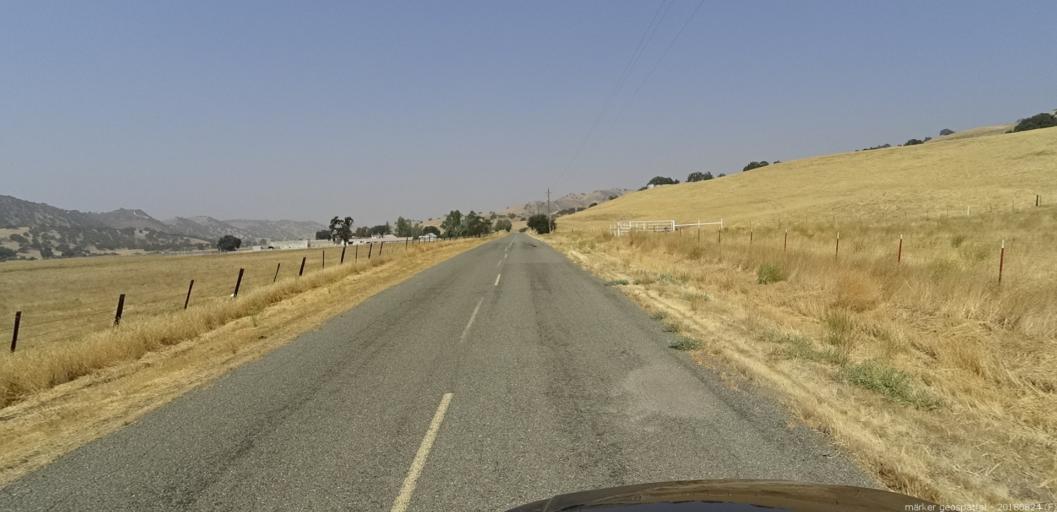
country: US
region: California
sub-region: Monterey County
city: King City
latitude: 36.1831
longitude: -120.8007
